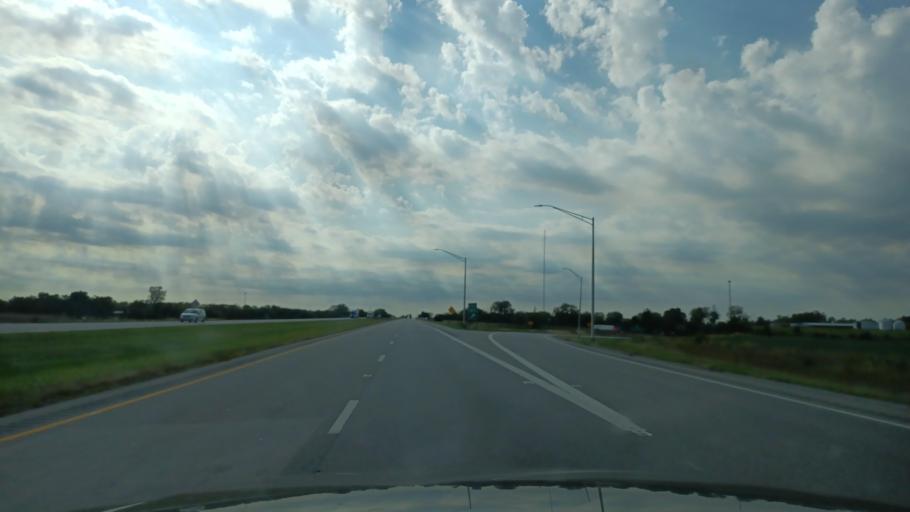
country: US
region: Ohio
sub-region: Fayette County
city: Washington Court House
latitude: 39.5146
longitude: -83.4039
